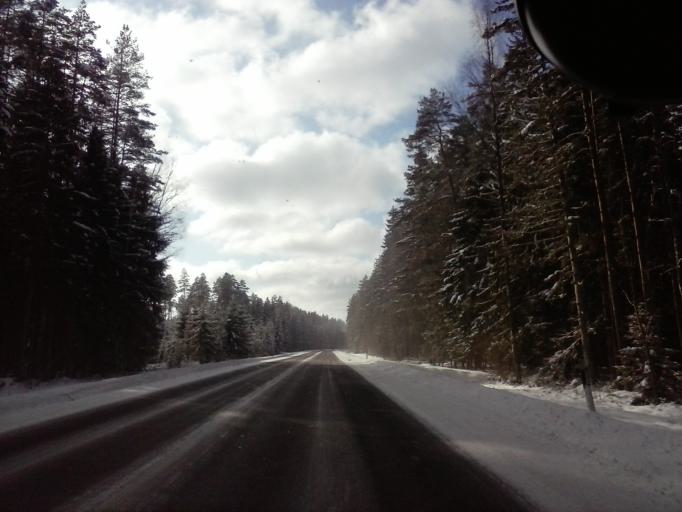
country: EE
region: Viljandimaa
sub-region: Moisakuela linn
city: Moisakula
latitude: 58.2263
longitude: 25.1091
